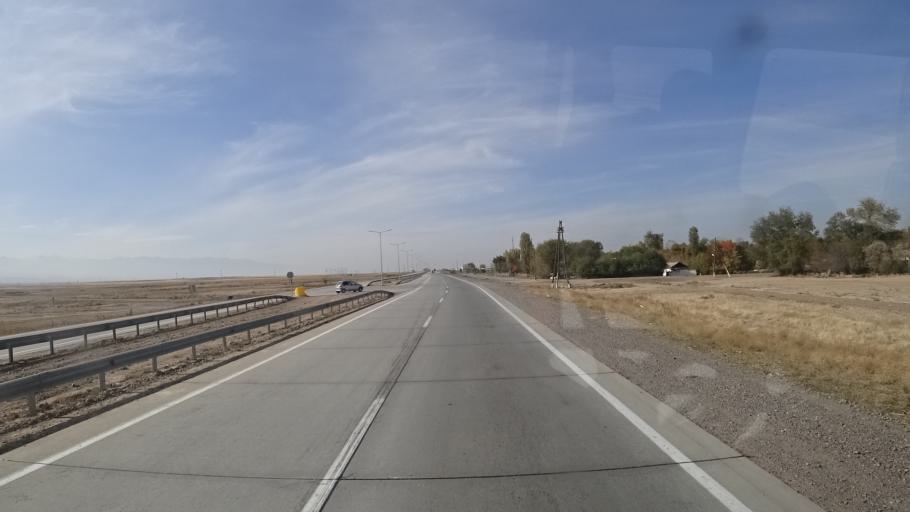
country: KZ
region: Zhambyl
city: Merke
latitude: 42.8885
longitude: 72.9954
